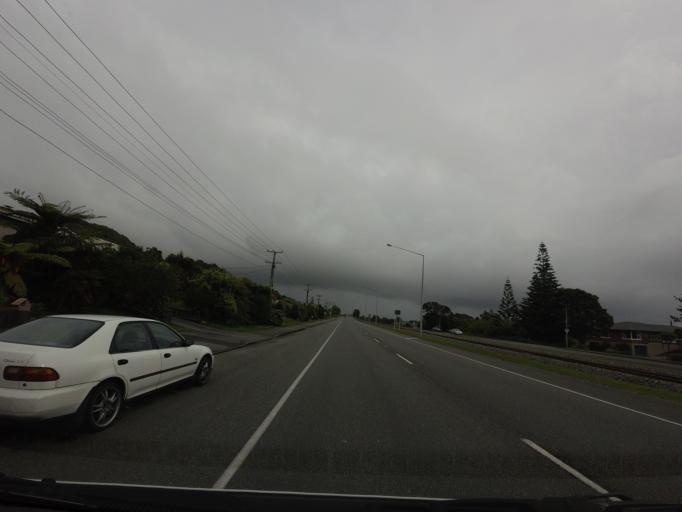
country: NZ
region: West Coast
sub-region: Grey District
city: Greymouth
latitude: -42.4731
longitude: 171.1876
